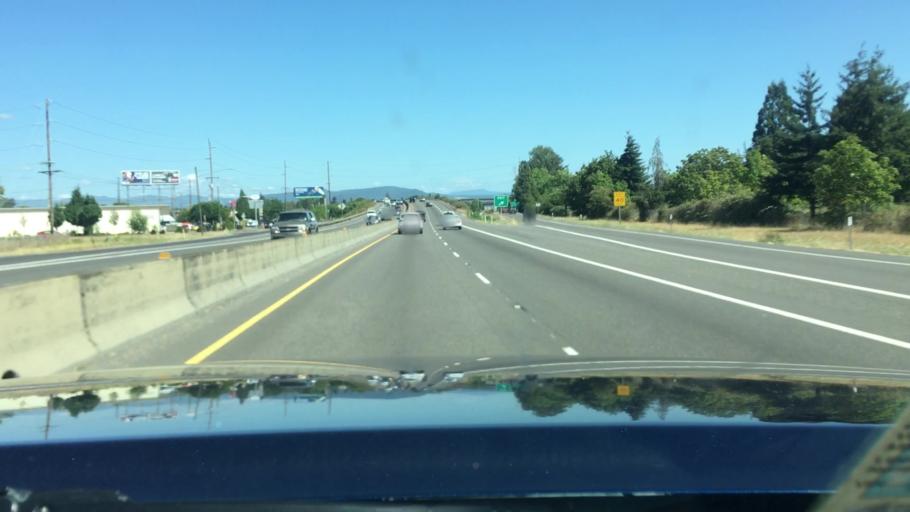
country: US
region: Oregon
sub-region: Lane County
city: Springfield
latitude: 44.0621
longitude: -123.0310
